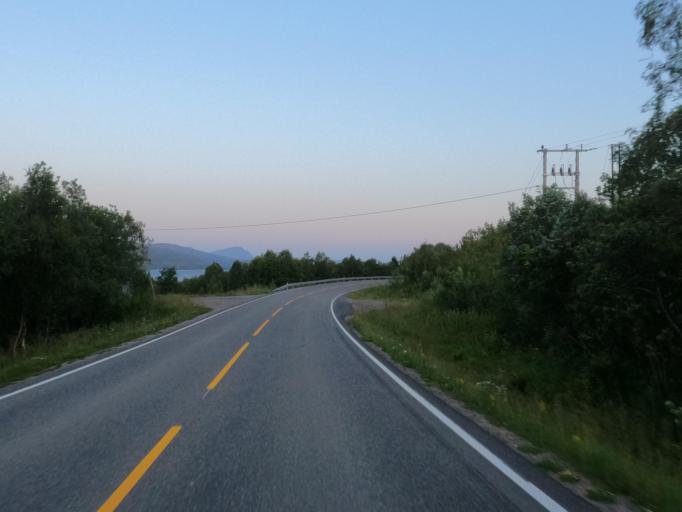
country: NO
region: Nordland
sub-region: Lodingen
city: Lodingen
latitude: 68.5167
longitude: 16.1044
